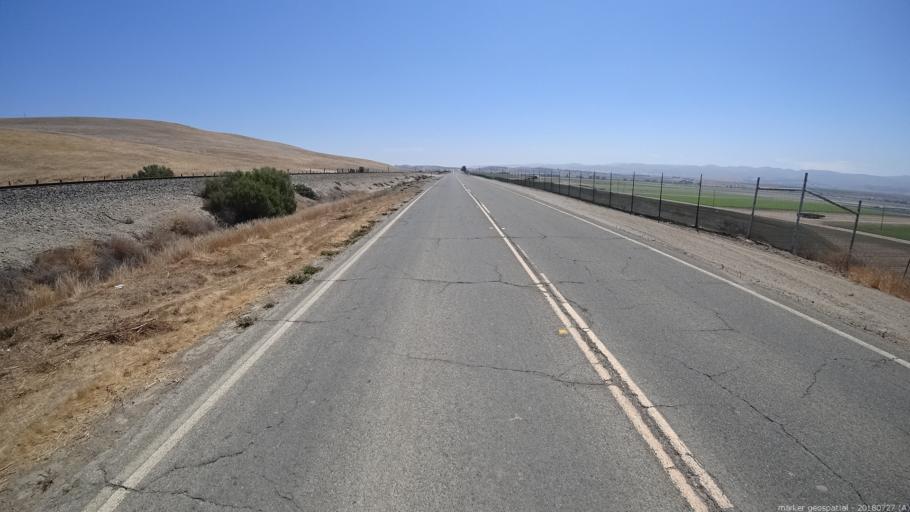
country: US
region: California
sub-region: Monterey County
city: King City
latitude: 36.1161
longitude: -121.0005
